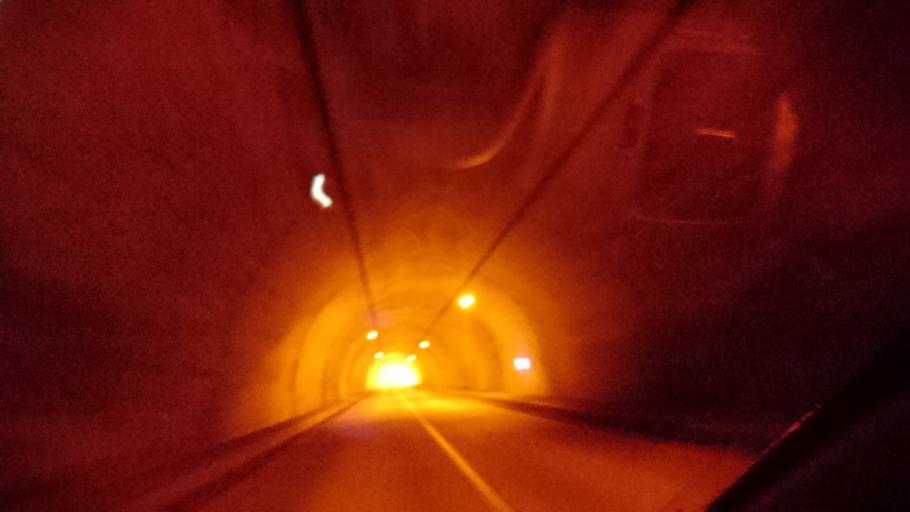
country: JP
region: Iwate
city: Mizusawa
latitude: 39.1228
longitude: 140.9067
